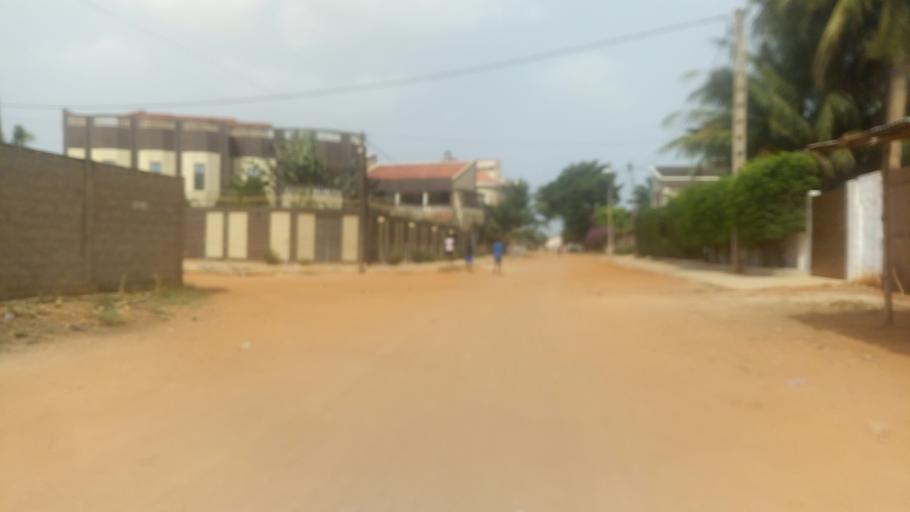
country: TG
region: Maritime
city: Lome
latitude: 6.1750
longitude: 1.1890
